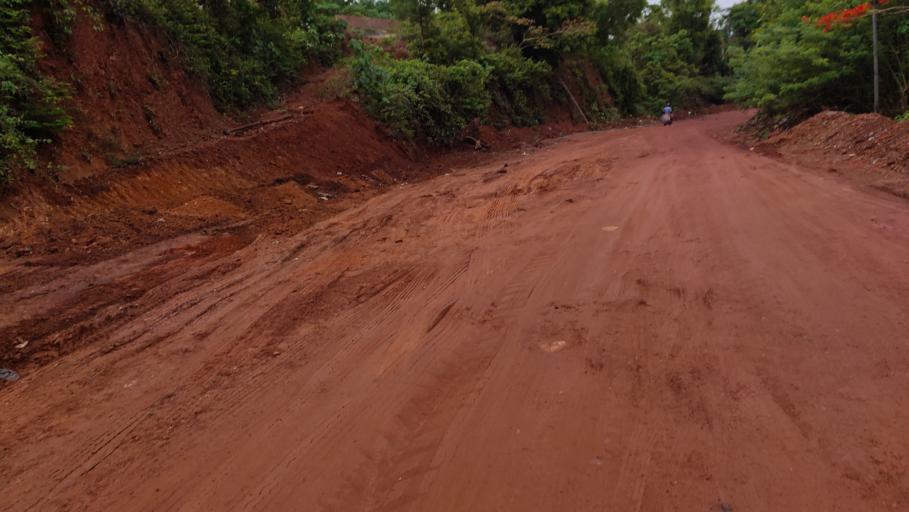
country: IN
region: Kerala
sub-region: Kasaragod District
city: Kasaragod
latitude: 12.5314
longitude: 75.0713
